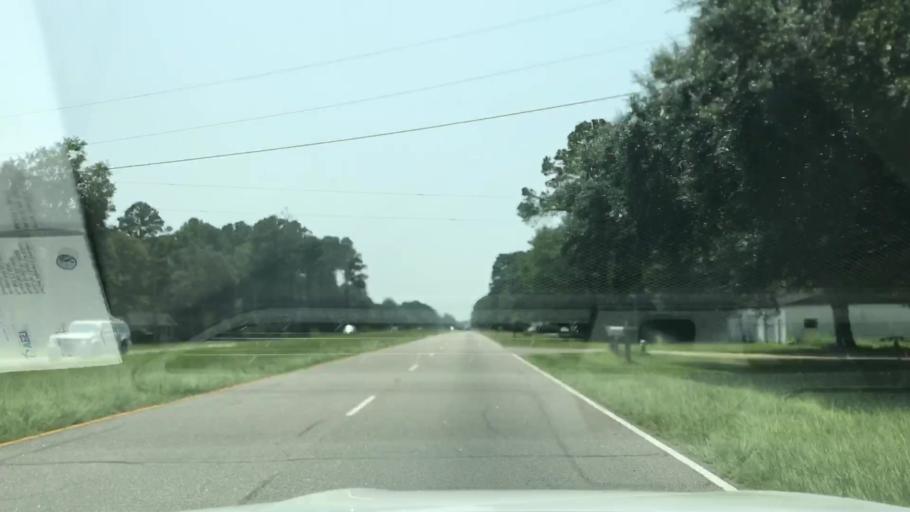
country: US
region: South Carolina
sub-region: Georgetown County
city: Georgetown
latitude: 33.3144
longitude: -79.3282
